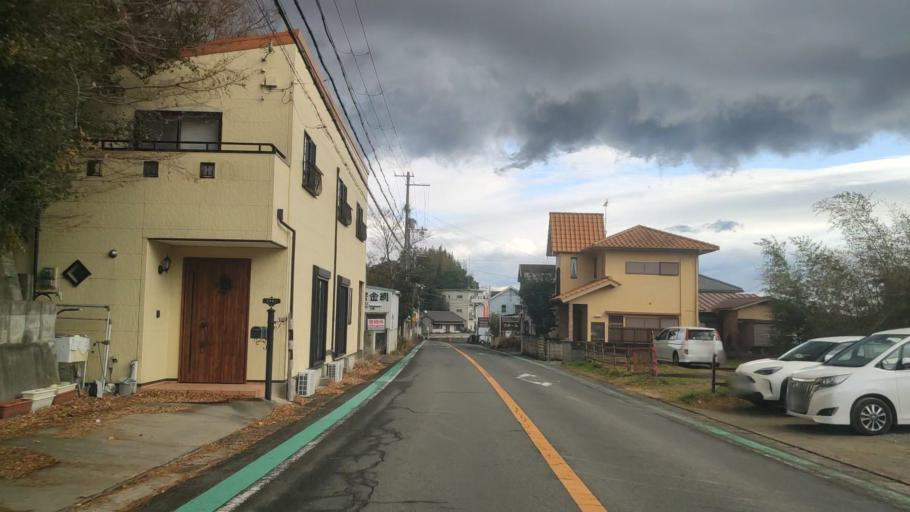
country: JP
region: Hyogo
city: Sumoto
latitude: 34.3269
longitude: 134.8583
